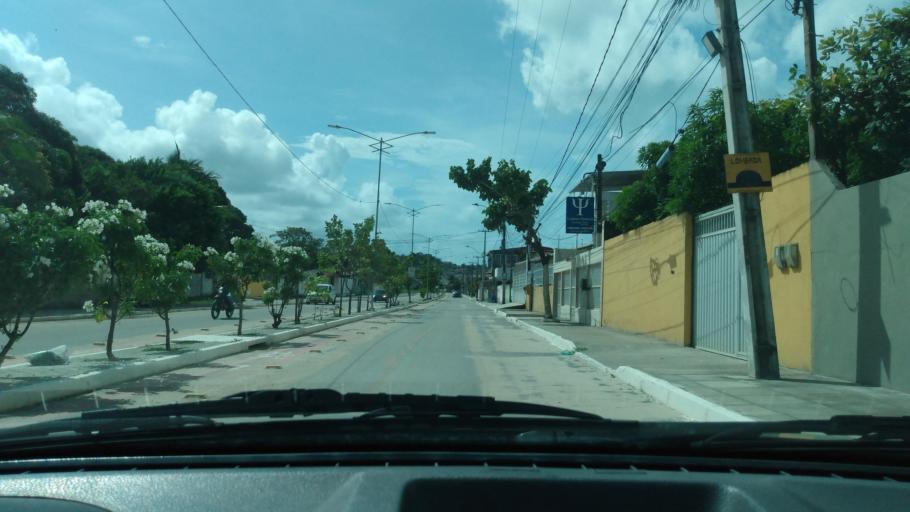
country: BR
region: Pernambuco
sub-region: Cabo De Santo Agostinho
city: Cabo
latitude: -8.3242
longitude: -34.9532
